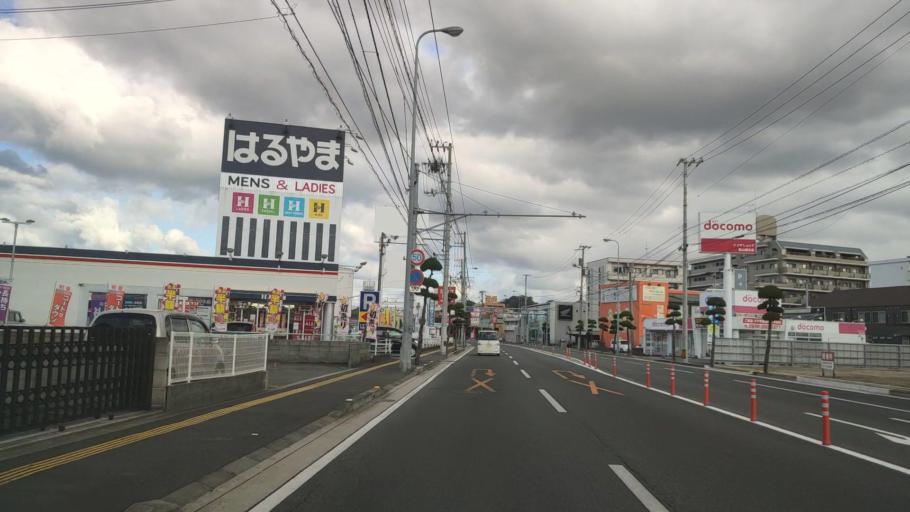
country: JP
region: Ehime
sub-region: Shikoku-chuo Shi
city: Matsuyama
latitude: 33.8689
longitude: 132.7519
